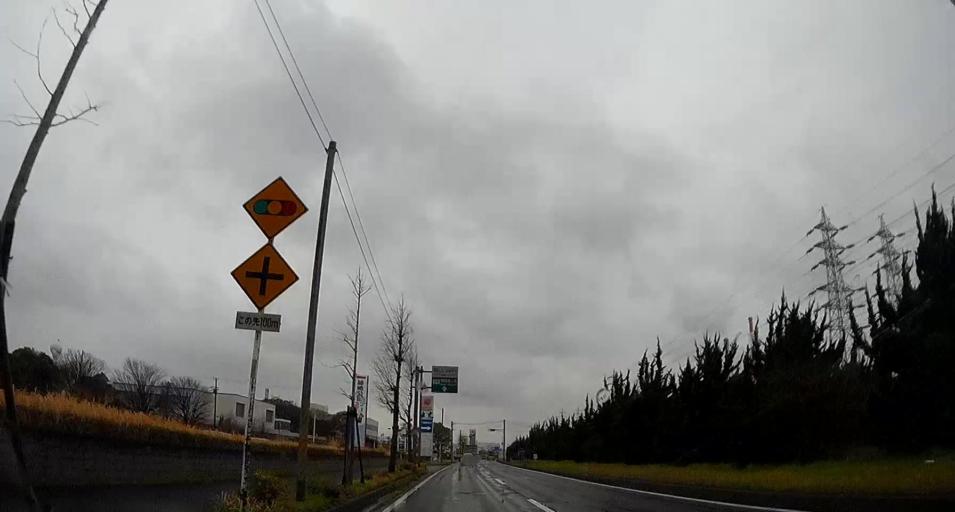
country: JP
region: Chiba
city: Ichihara
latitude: 35.4895
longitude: 140.0427
